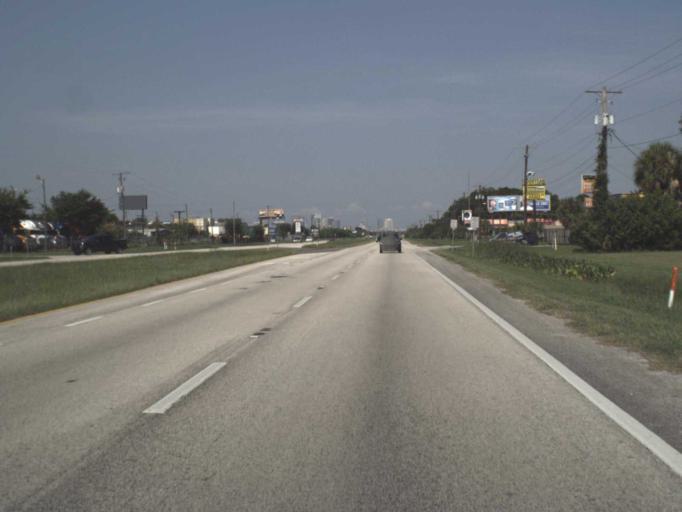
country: US
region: Florida
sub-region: Hillsborough County
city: Palm River-Clair Mel
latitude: 27.9523
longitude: -82.3869
